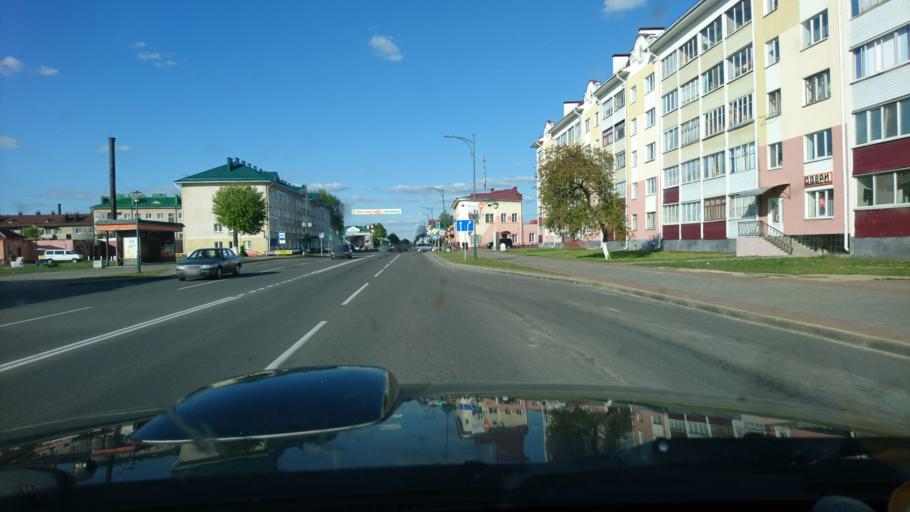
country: BY
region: Brest
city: Byaroza
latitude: 52.5329
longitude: 24.9820
